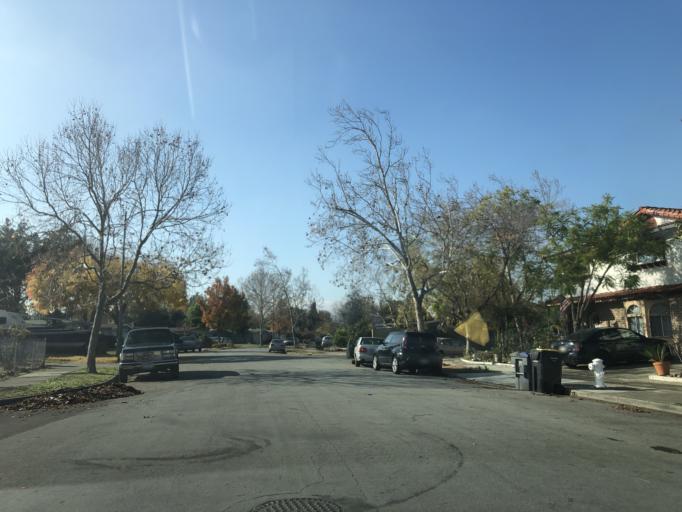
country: US
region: California
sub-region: Santa Clara County
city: Sunnyvale
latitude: 37.3975
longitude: -122.0050
